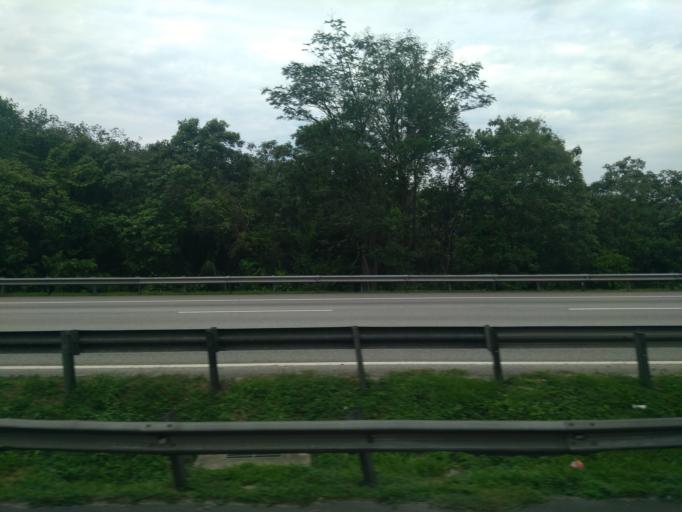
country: MY
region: Negeri Sembilan
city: Tampin
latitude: 2.4667
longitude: 102.1473
